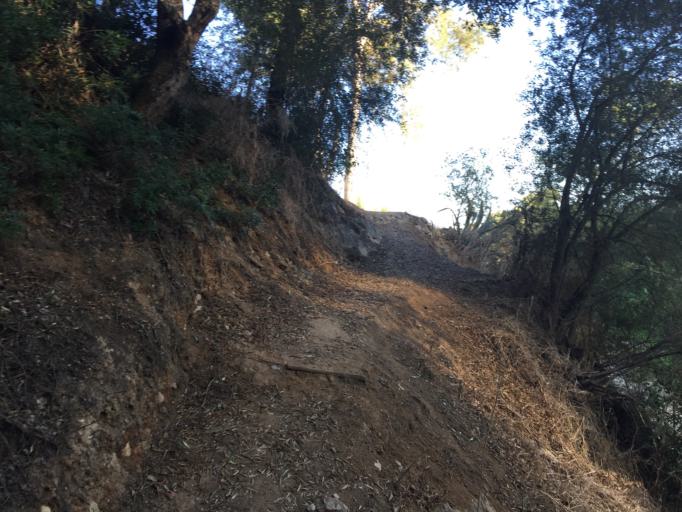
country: PT
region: Lisbon
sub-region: Alenquer
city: Alenquer
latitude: 39.1132
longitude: -8.9952
